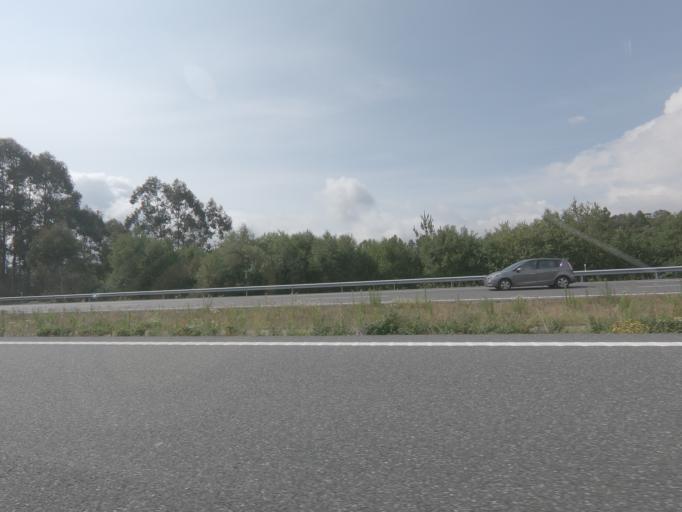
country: ES
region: Galicia
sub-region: Provincia de Pontevedra
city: Covelo
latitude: 42.2001
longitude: -8.2951
